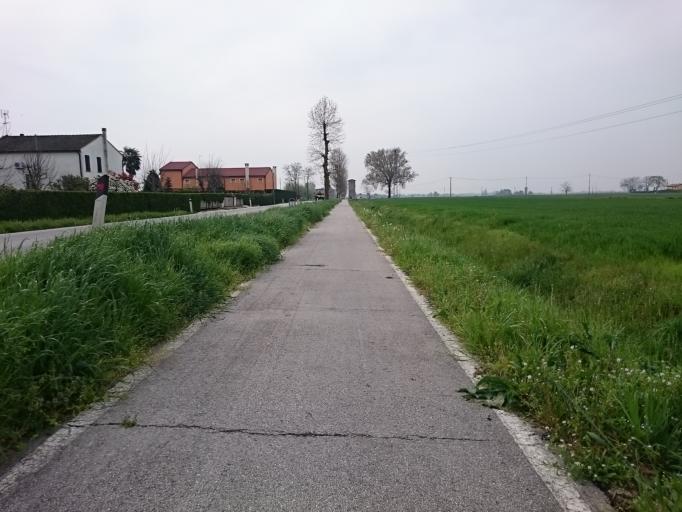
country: IT
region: Veneto
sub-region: Provincia di Padova
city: Bagnoli di Sopra
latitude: 45.1756
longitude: 11.8800
